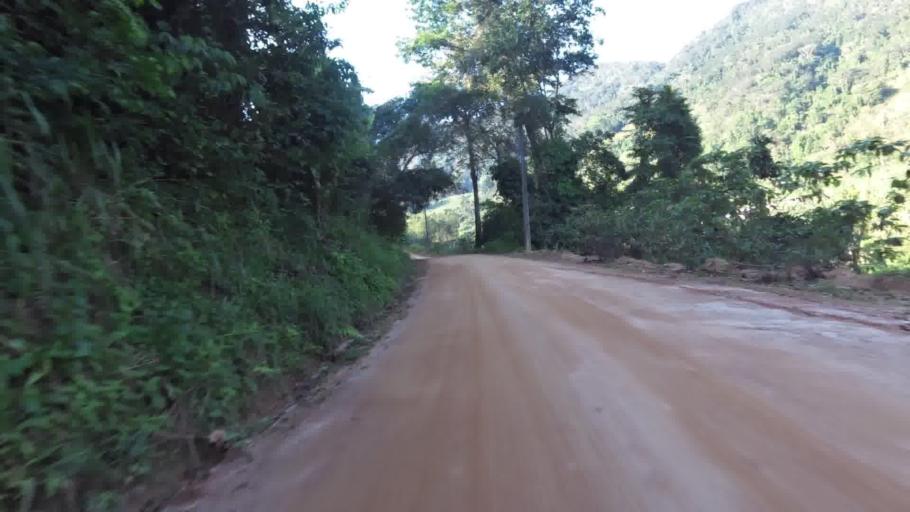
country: BR
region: Espirito Santo
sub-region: Alfredo Chaves
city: Alfredo Chaves
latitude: -20.5745
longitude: -40.6975
